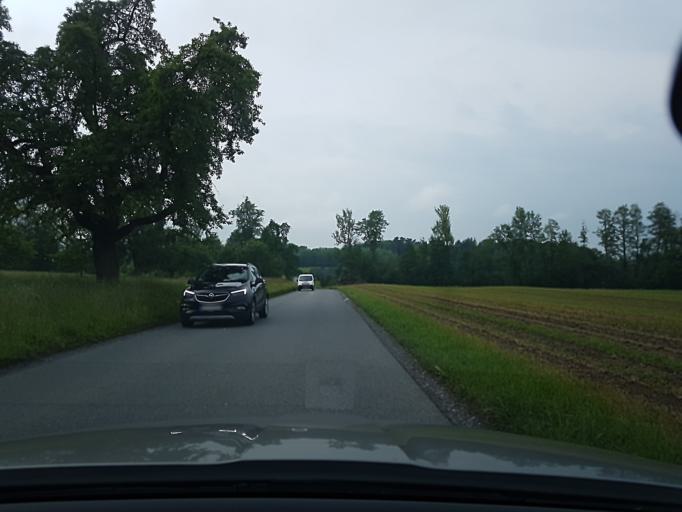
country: CH
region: Thurgau
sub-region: Arbon District
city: Roggwil
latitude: 47.5041
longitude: 9.3921
